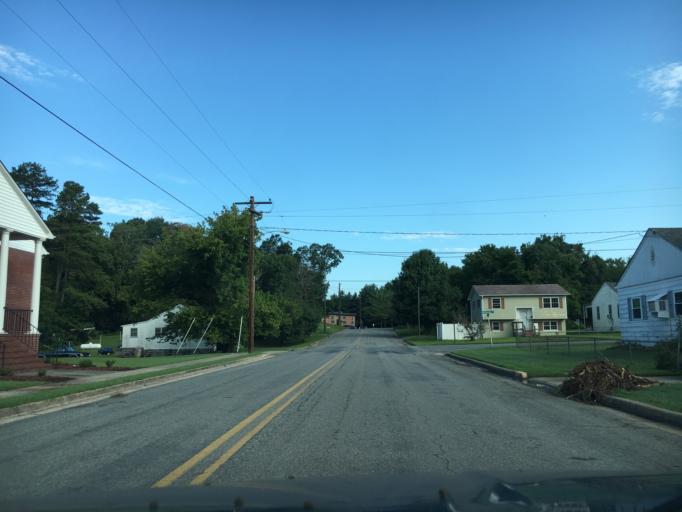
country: US
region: Virginia
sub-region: Halifax County
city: South Boston
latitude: 36.7032
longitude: -78.9116
